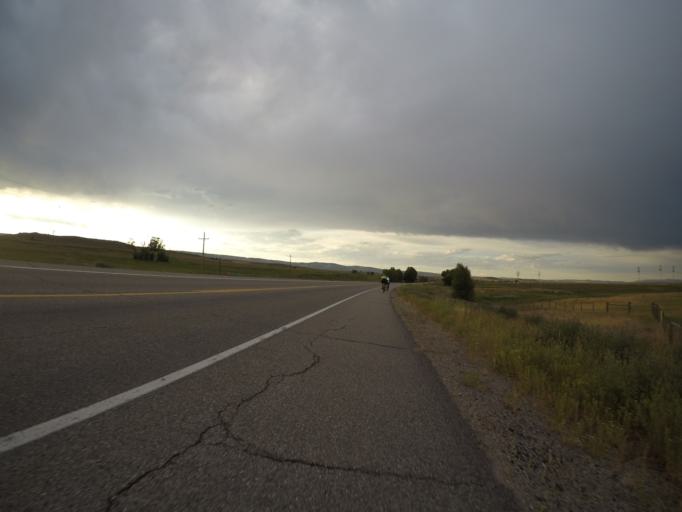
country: US
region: Idaho
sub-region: Bear Lake County
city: Montpelier
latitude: 42.0660
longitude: -110.9380
